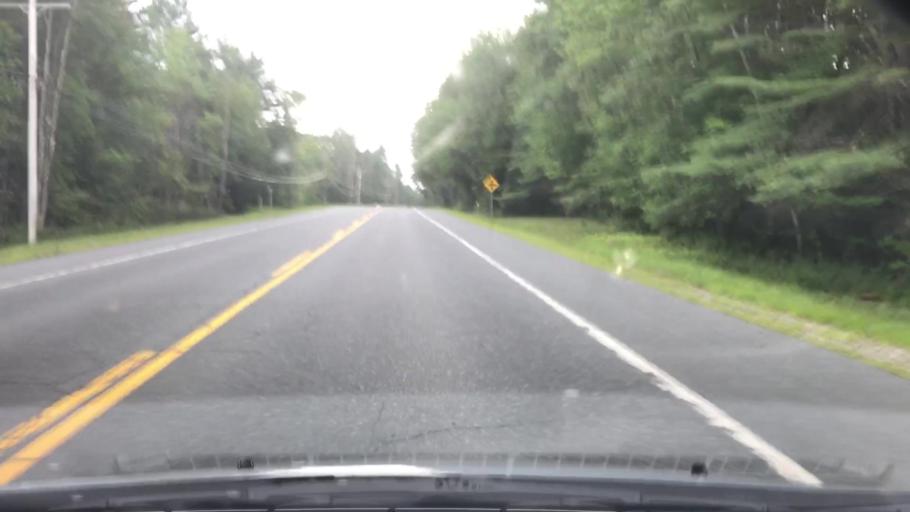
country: US
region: New Hampshire
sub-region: Grafton County
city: Lyme
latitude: 43.7853
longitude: -72.1764
